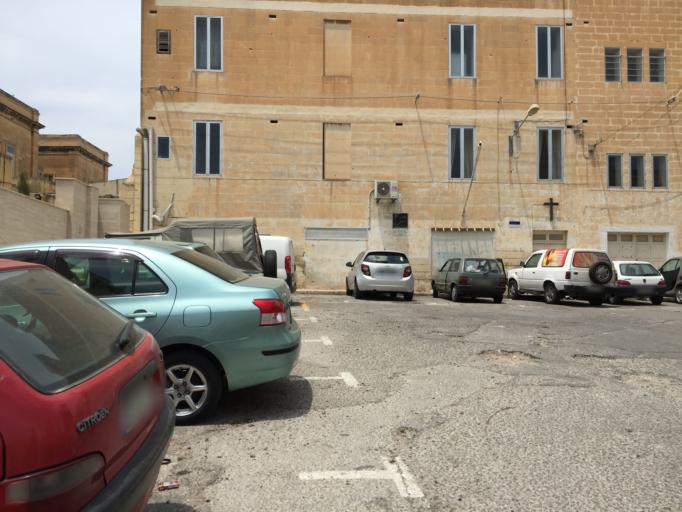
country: MT
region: Il-Hamrun
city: Hamrun
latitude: 35.8881
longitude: 14.4888
